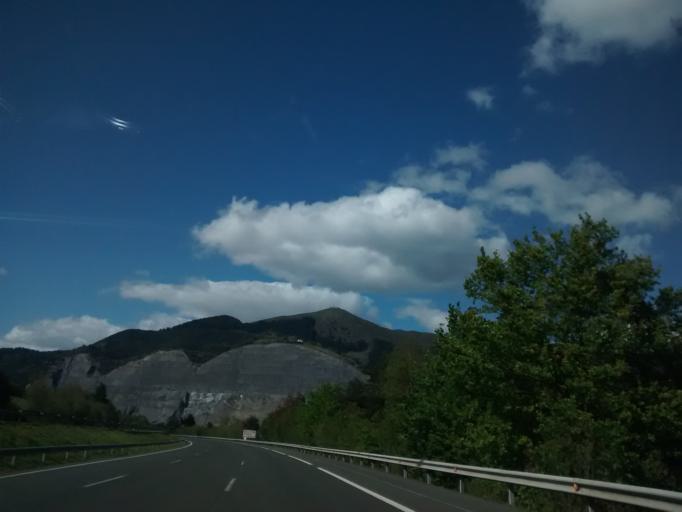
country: ES
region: Basque Country
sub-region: Bizkaia
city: Elexalde
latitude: 43.1111
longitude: -2.9143
